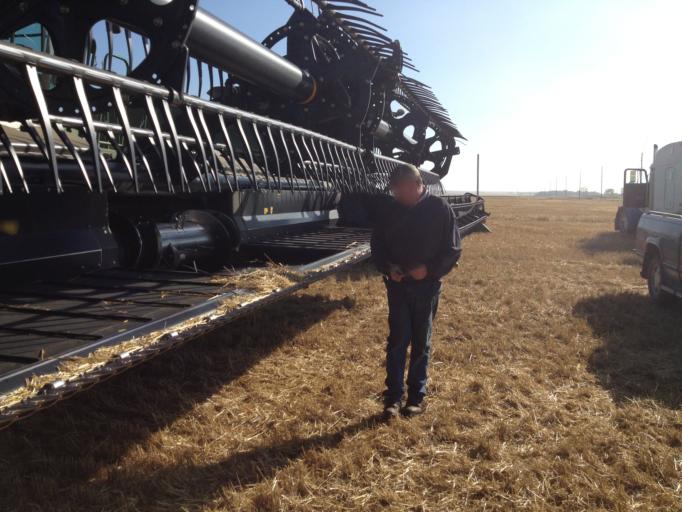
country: US
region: North Dakota
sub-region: McLean County
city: Garrison
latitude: 47.7178
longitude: -101.7962
